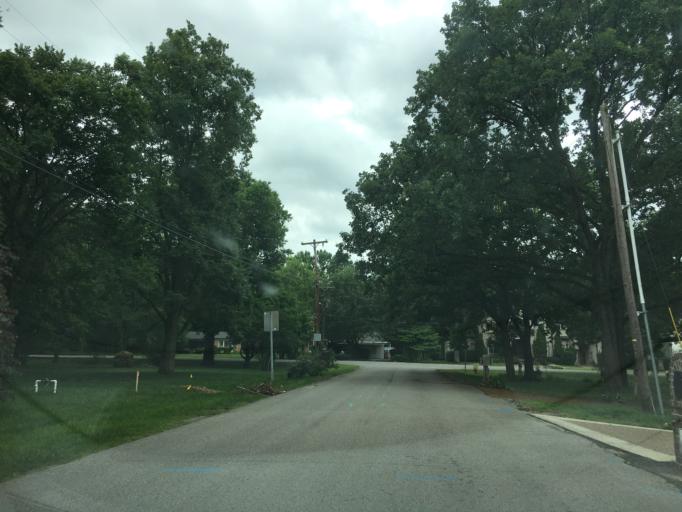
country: US
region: Tennessee
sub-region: Davidson County
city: Belle Meade
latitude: 36.0955
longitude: -86.8415
